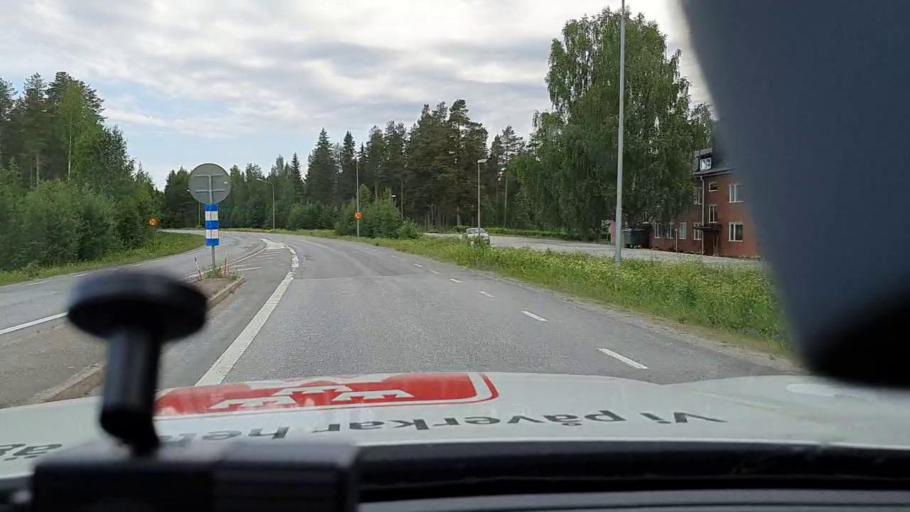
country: SE
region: Norrbotten
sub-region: Bodens Kommun
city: Boden
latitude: 65.8154
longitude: 21.6466
